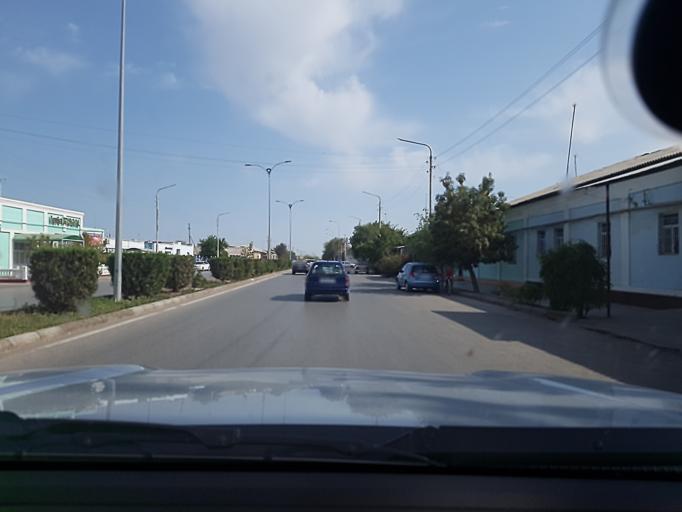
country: TM
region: Dasoguz
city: Dasoguz
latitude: 41.8324
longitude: 59.9829
